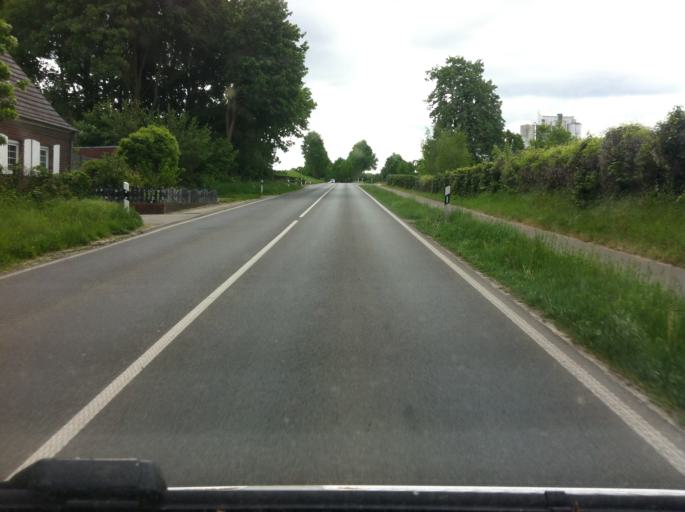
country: DE
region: North Rhine-Westphalia
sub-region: Regierungsbezirk Dusseldorf
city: Bruggen
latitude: 51.2322
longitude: 6.1928
